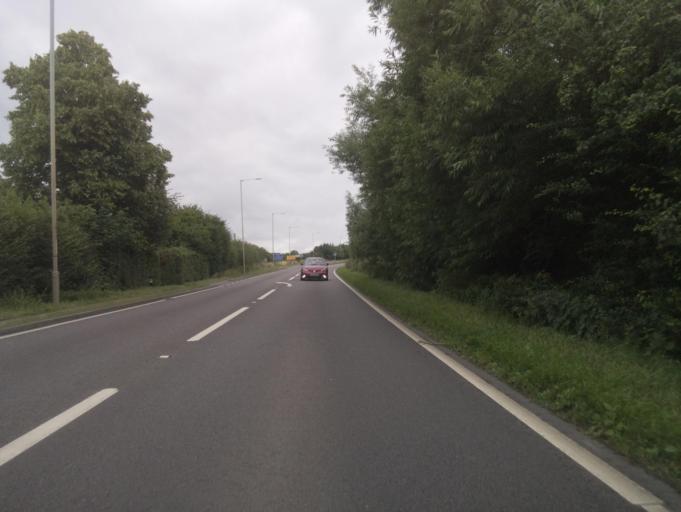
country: GB
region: England
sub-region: Lincolnshire
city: Barrowby
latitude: 52.9236
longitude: -0.6932
